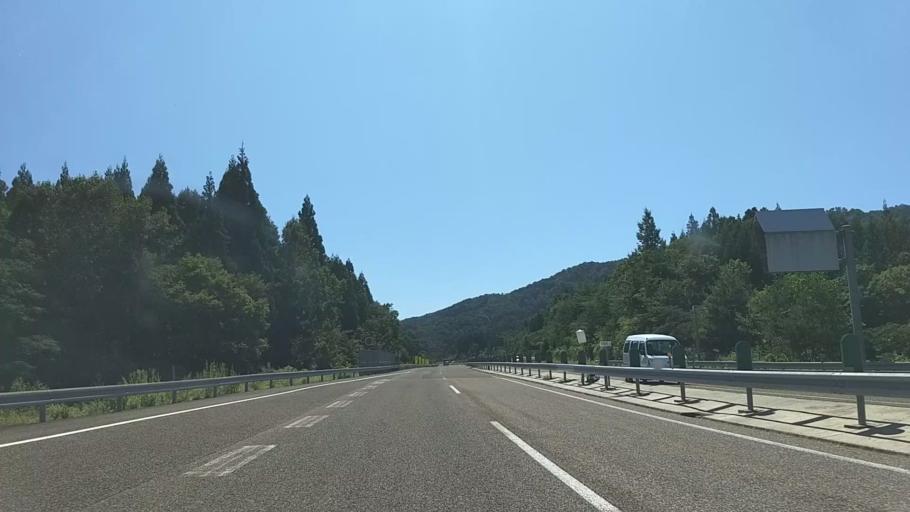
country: JP
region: Niigata
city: Joetsu
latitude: 37.0845
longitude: 138.2258
